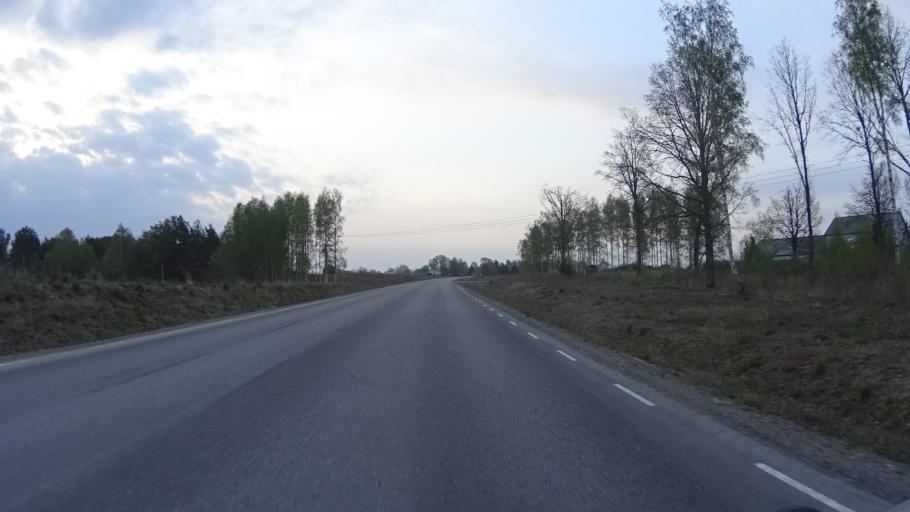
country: SE
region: Vaestra Goetaland
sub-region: Gotene Kommun
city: Kallby
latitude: 58.4977
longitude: 13.3068
